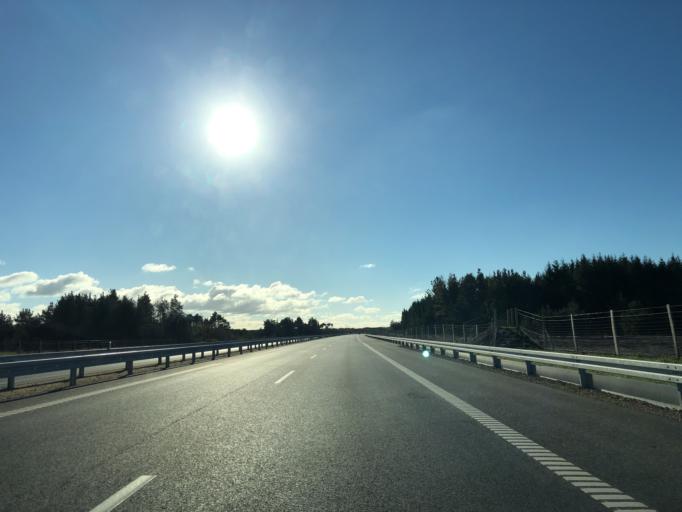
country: DK
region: Central Jutland
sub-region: Herning Kommune
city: Avlum
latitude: 56.3373
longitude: 8.7376
